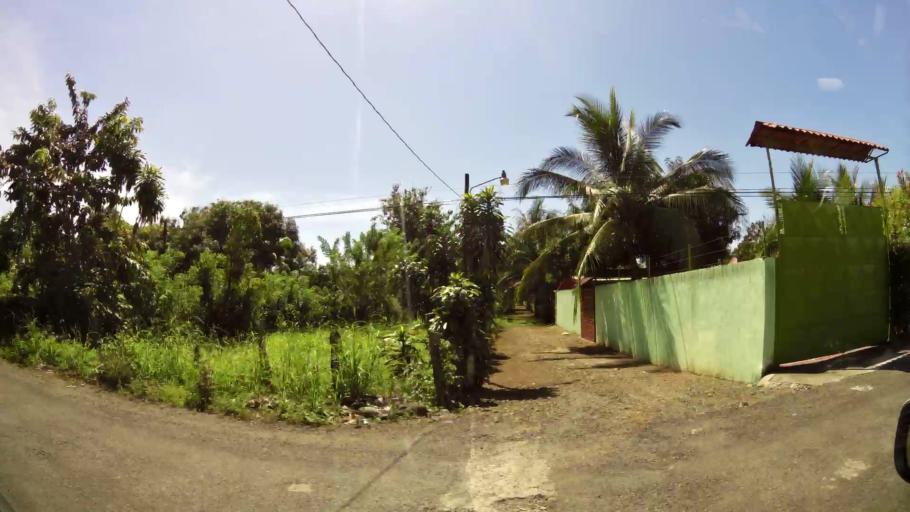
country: CR
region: Puntarenas
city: Quepos
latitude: 9.3299
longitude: -83.9554
